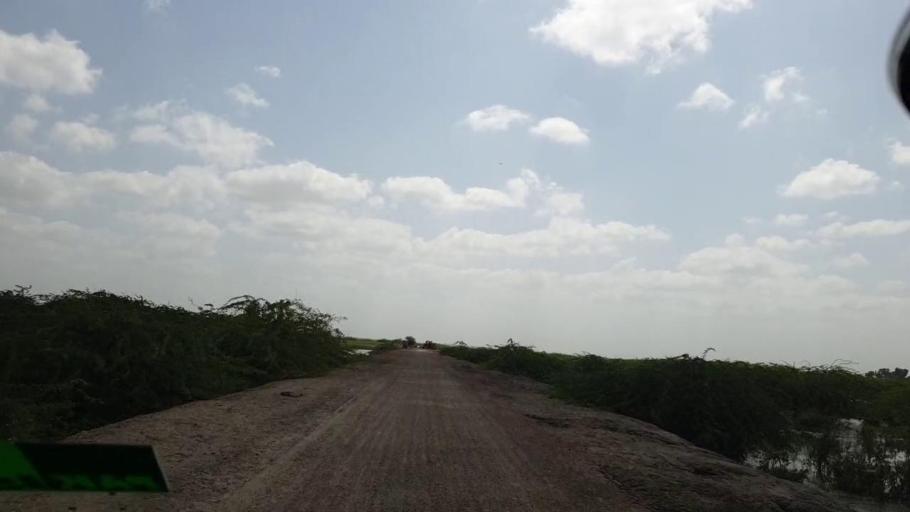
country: PK
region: Sindh
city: Kadhan
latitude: 24.5918
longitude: 69.1831
